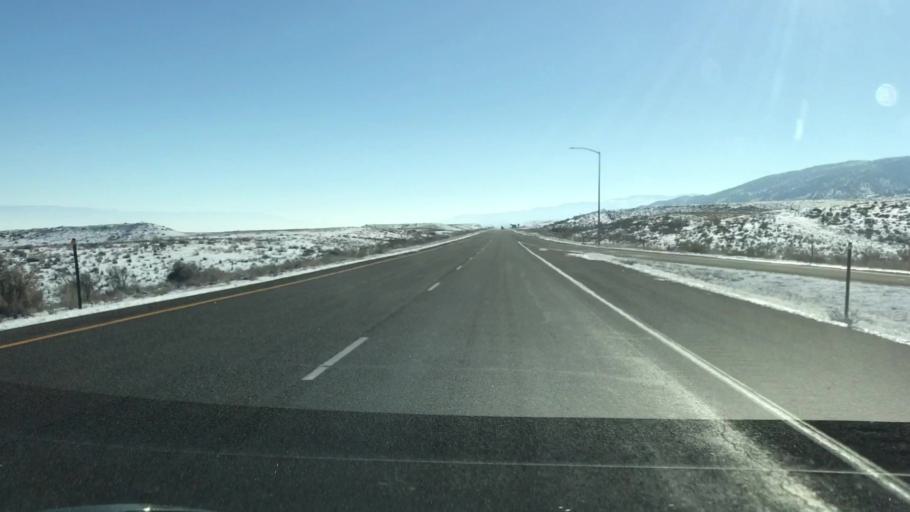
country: US
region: Colorado
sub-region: Mesa County
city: Loma
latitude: 39.2112
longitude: -108.8654
